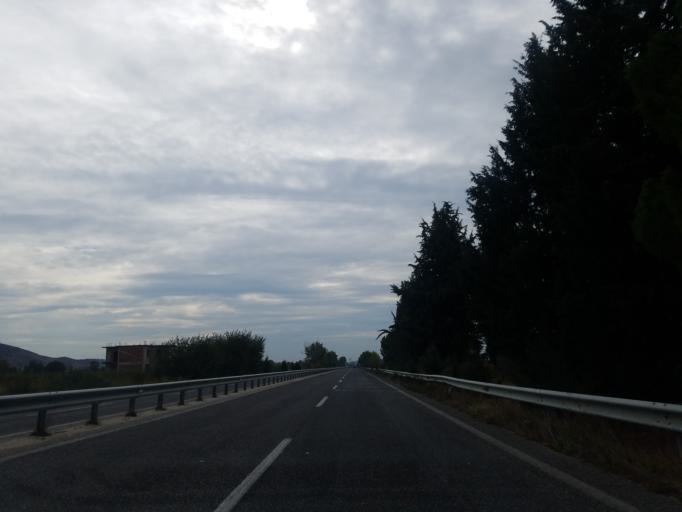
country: GR
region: Thessaly
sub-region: Trikala
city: Vasiliki
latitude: 39.6413
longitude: 21.6931
